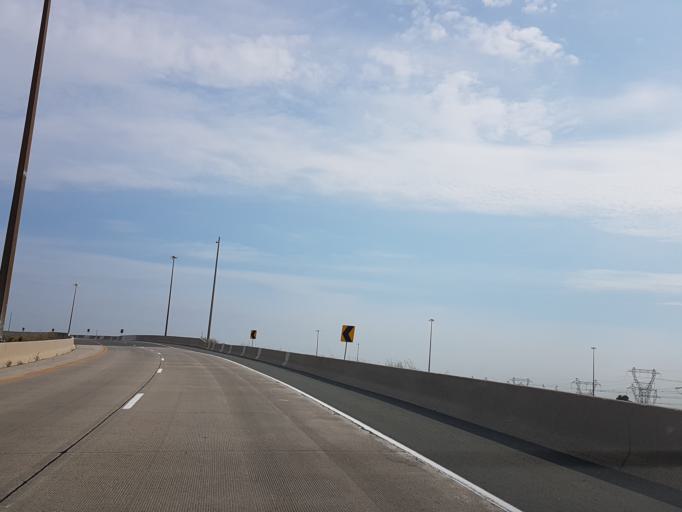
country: CA
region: Ontario
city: Brampton
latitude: 43.6654
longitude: -79.7015
